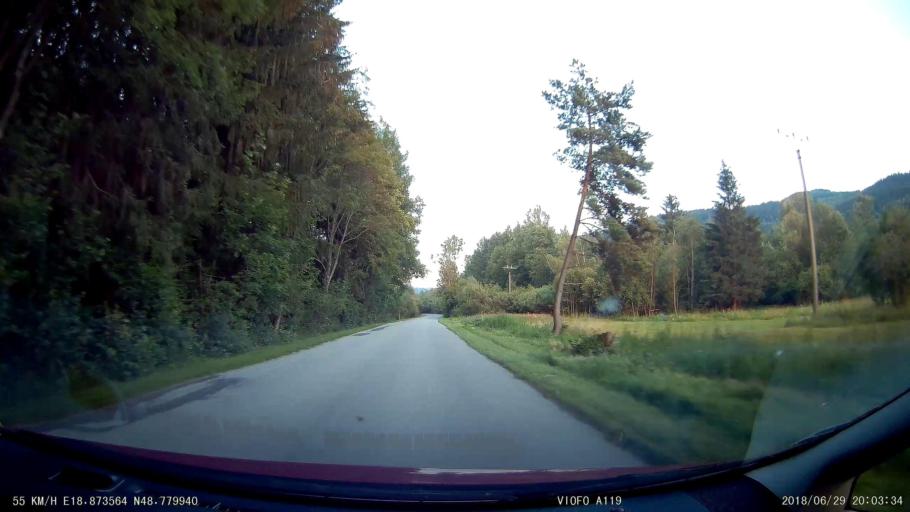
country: SK
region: Banskobystricky
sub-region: Okres Ziar nad Hronom
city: Kremnica
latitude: 48.7799
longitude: 18.8738
